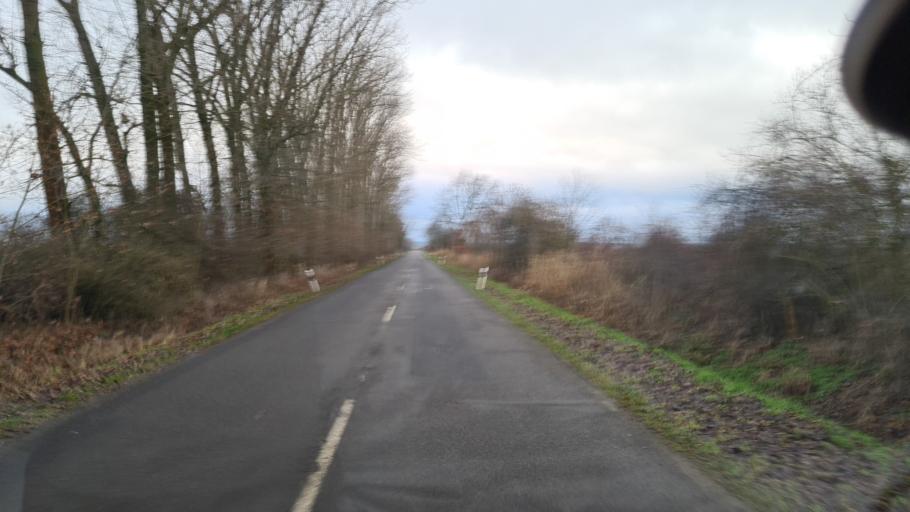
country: DE
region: Brandenburg
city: Vogelsang
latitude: 52.2257
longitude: 14.6691
